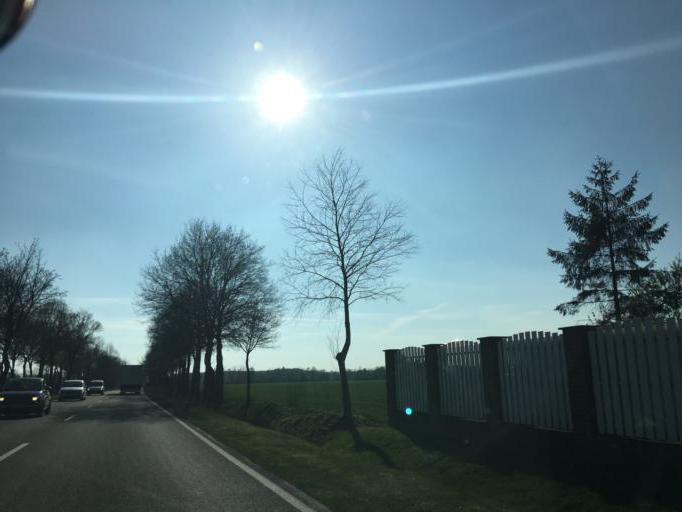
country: DE
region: North Rhine-Westphalia
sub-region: Regierungsbezirk Munster
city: Saerbeck
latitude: 52.1218
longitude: 7.6555
